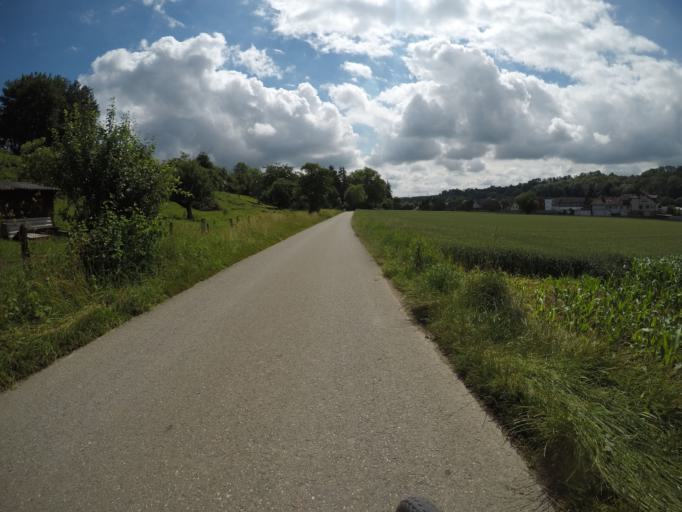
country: DE
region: Baden-Wuerttemberg
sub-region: Regierungsbezirk Stuttgart
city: Ebersbach an der Fils
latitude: 48.7155
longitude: 9.5099
